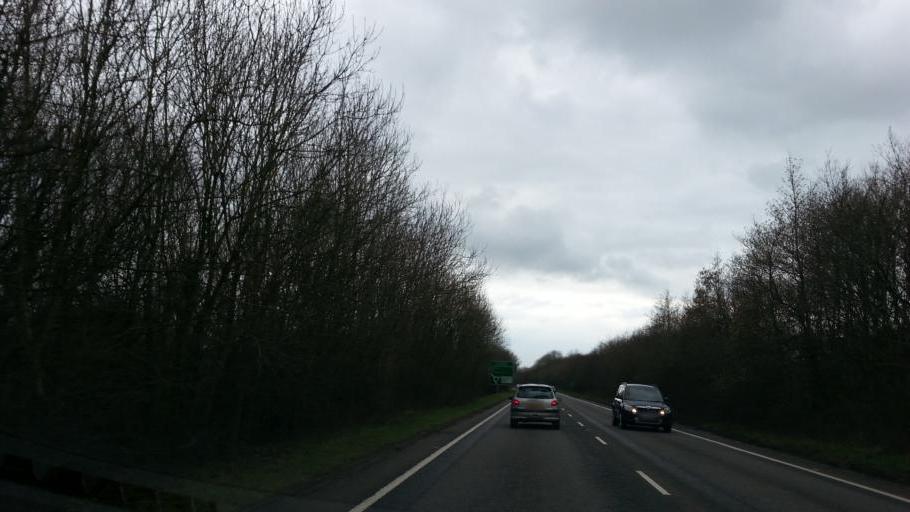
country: GB
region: England
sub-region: Devon
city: Barnstaple
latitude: 51.0710
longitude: -4.0255
